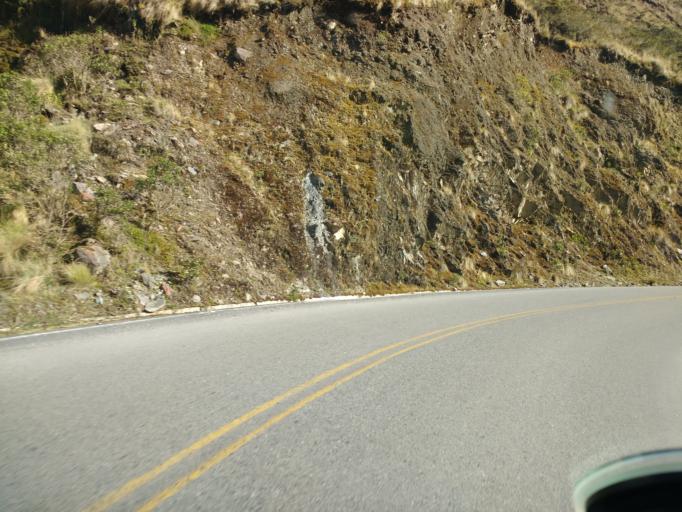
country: PE
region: Cusco
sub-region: Provincia de Urubamba
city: Ollantaytambo
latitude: -13.1215
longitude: -72.3261
